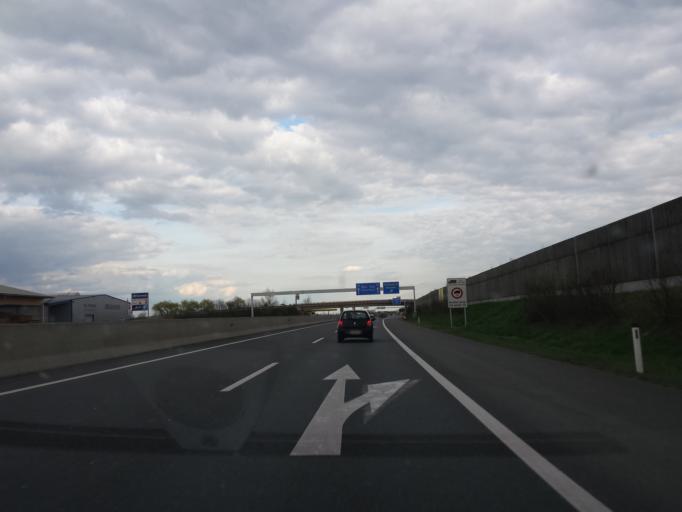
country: AT
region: Lower Austria
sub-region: Politischer Bezirk Tulln
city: Grafenworth
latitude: 48.4118
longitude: 15.7714
